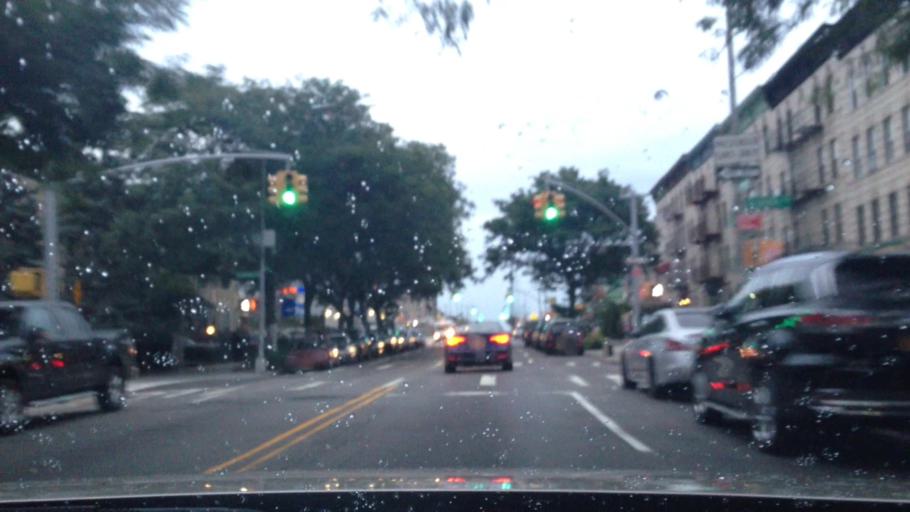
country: US
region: New York
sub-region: Kings County
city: East New York
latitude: 40.6834
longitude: -73.9075
